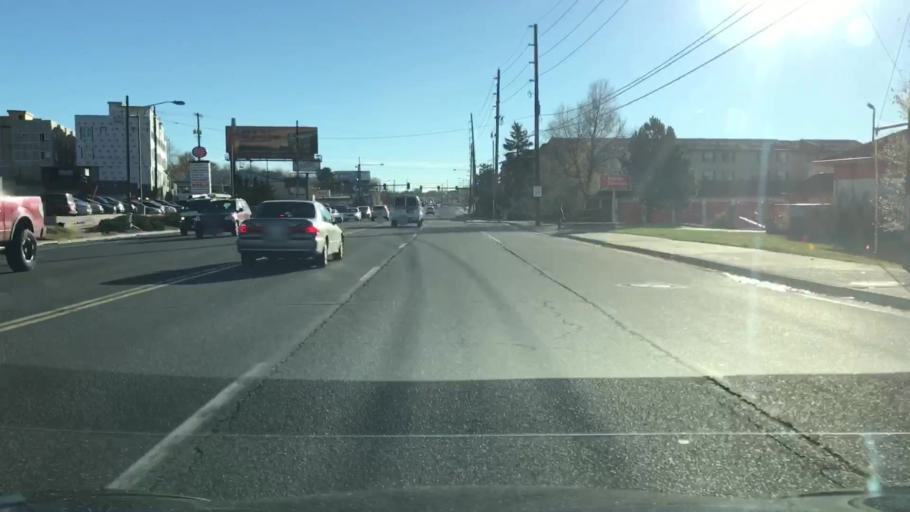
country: US
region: Colorado
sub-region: Arapahoe County
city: Glendale
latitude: 39.7084
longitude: -104.9292
